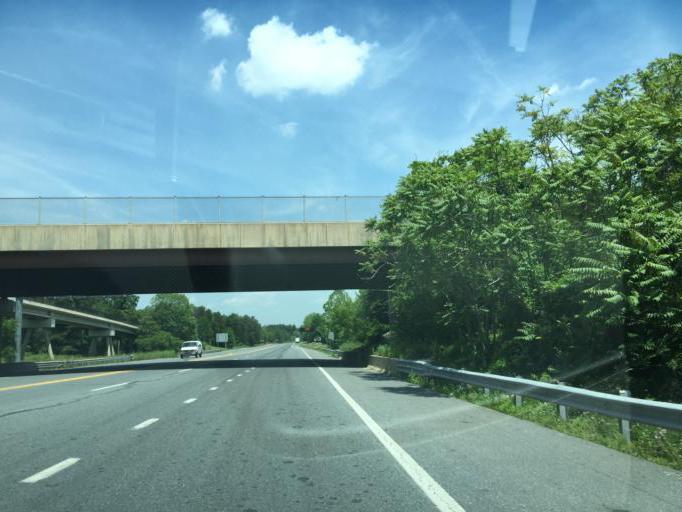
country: US
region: Maryland
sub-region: Howard County
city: Hanover
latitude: 39.1775
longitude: -76.6929
